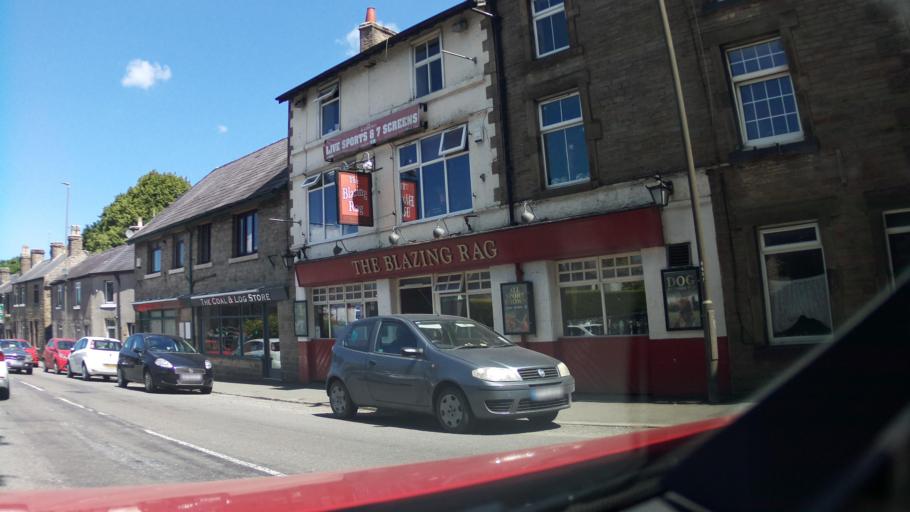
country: GB
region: England
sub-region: Derbyshire
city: Buxton
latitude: 53.2512
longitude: -1.9114
